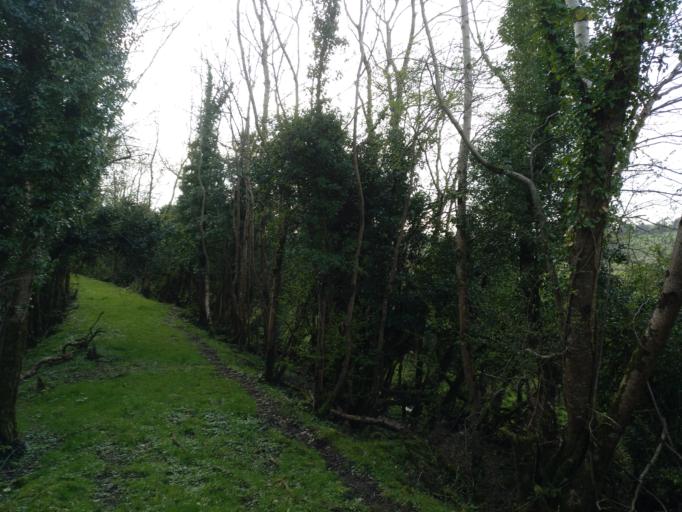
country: IE
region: Ulster
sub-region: County Monaghan
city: Clones
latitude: 54.1973
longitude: -7.1443
